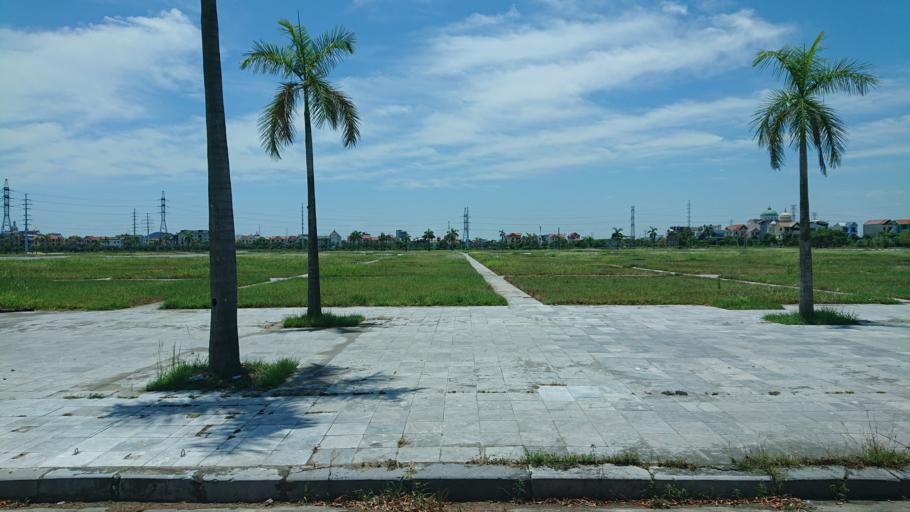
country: VN
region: Ninh Binh
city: Thanh Pho Ninh Binh
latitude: 20.2711
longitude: 105.9741
